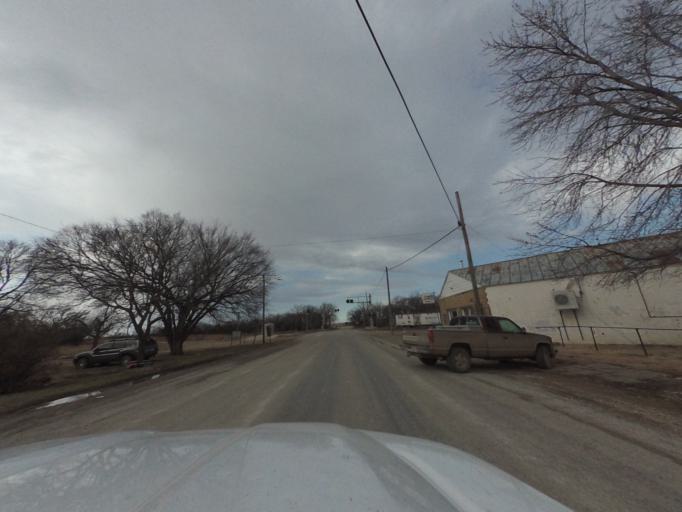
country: US
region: Kansas
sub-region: Chase County
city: Cottonwood Falls
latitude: 38.3735
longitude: -96.6469
